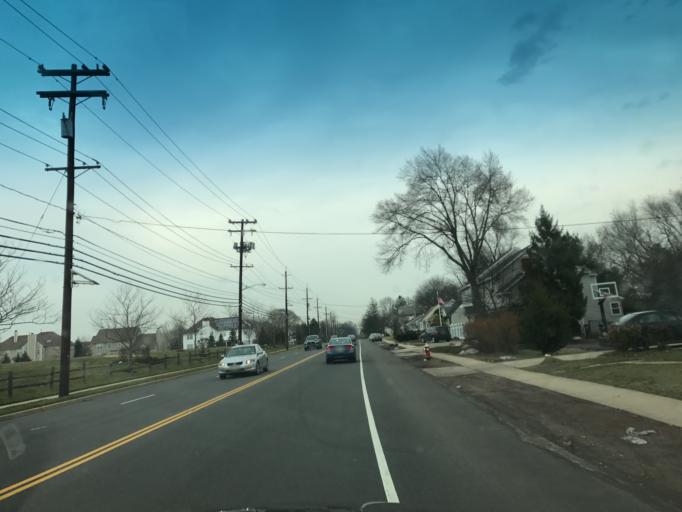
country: US
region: New Jersey
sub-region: Middlesex County
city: South River
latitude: 40.4407
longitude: -74.4028
